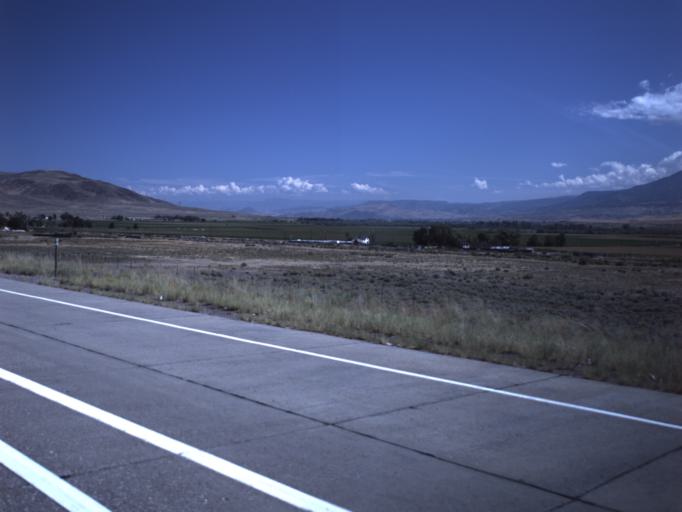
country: US
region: Utah
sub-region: Sevier County
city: Monroe
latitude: 38.6324
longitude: -112.2230
